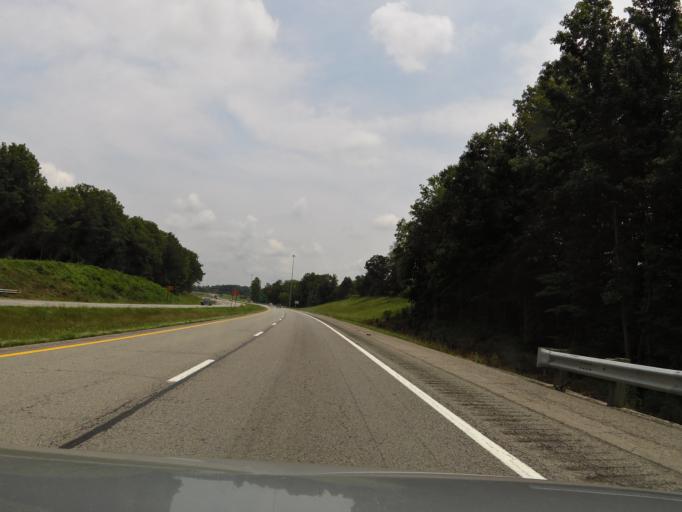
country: US
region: Kentucky
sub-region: Hardin County
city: Elizabethtown
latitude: 37.6494
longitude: -85.8991
